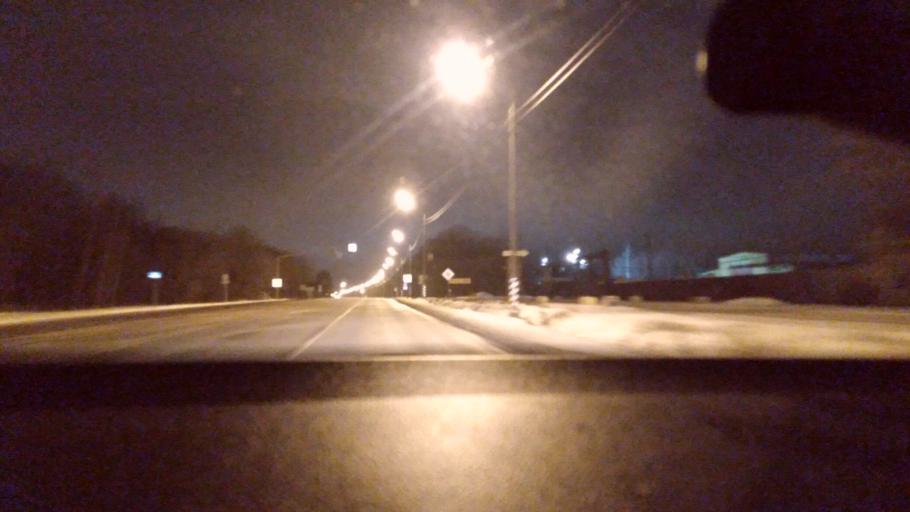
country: RU
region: Moskovskaya
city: Bronnitsy
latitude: 55.4745
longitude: 38.1886
